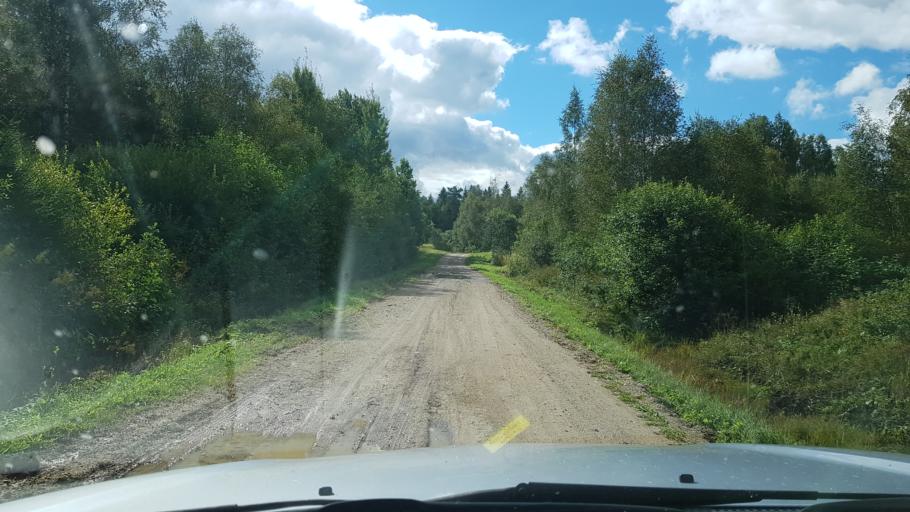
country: EE
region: Harju
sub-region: Raasiku vald
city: Arukula
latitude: 59.3128
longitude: 25.0744
